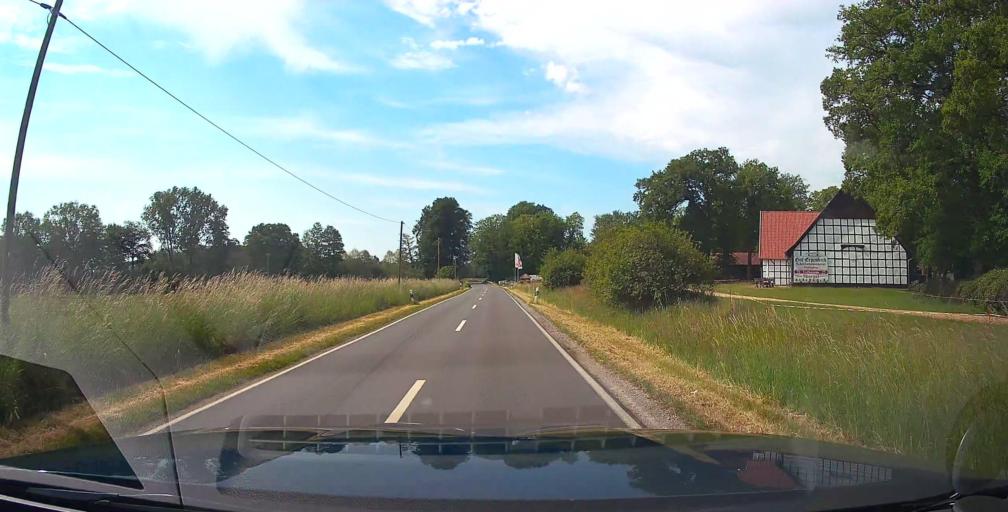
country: DE
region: North Rhine-Westphalia
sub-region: Regierungsbezirk Munster
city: Ladbergen
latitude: 52.1388
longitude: 7.7976
